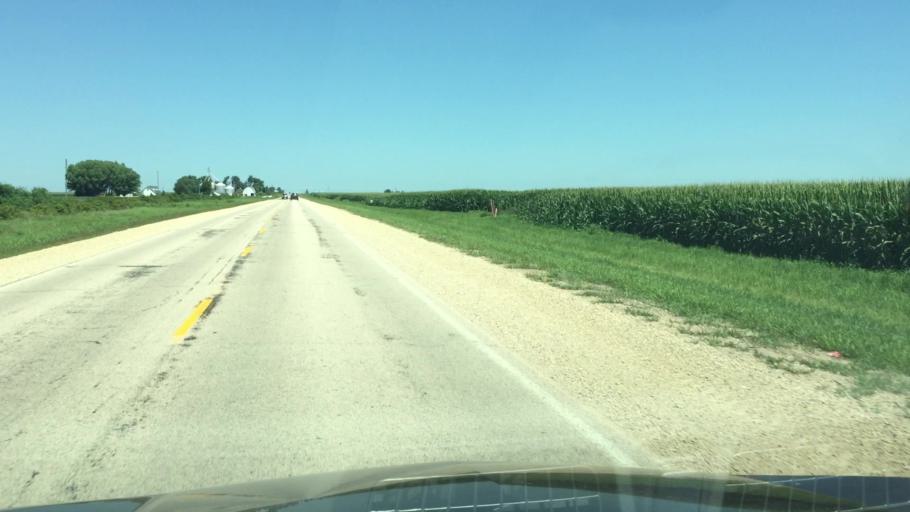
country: US
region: Iowa
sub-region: Cedar County
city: Mechanicsville
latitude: 41.9098
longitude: -91.1520
